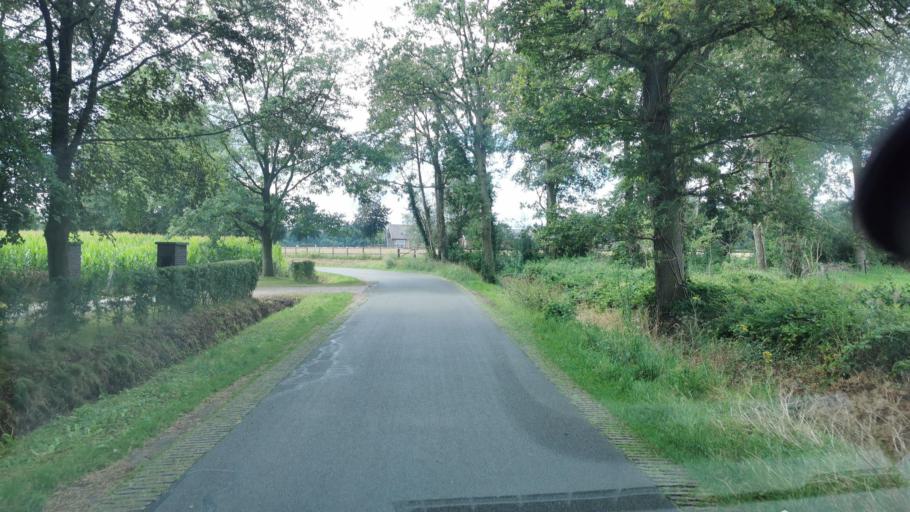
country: NL
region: Overijssel
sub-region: Gemeente Haaksbergen
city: Haaksbergen
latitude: 52.1467
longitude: 6.7128
